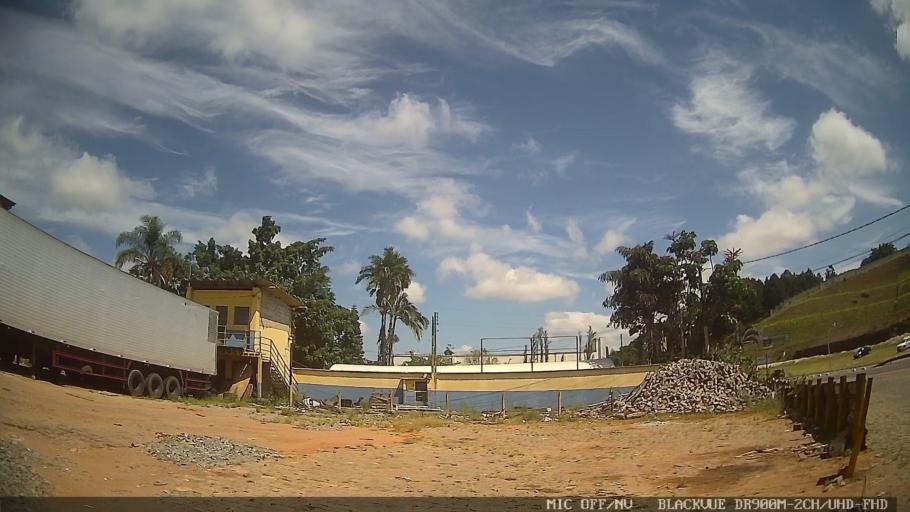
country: BR
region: Sao Paulo
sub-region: Braganca Paulista
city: Braganca Paulista
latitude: -22.9943
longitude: -46.5623
